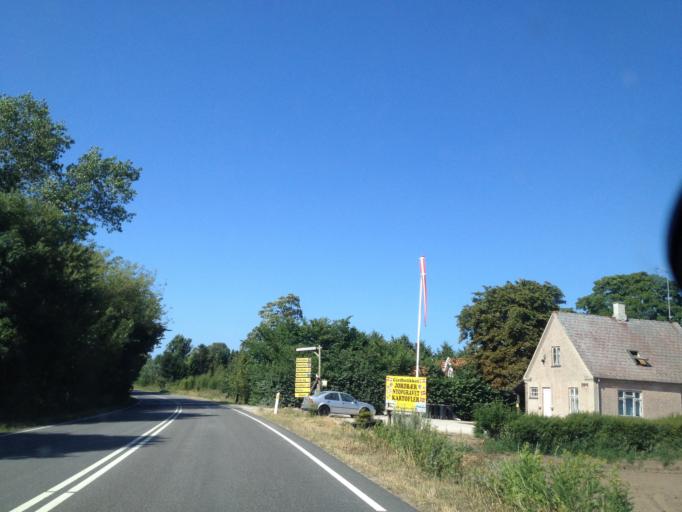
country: DK
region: Capital Region
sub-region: Gribskov Kommune
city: Graested
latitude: 56.0708
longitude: 12.3457
